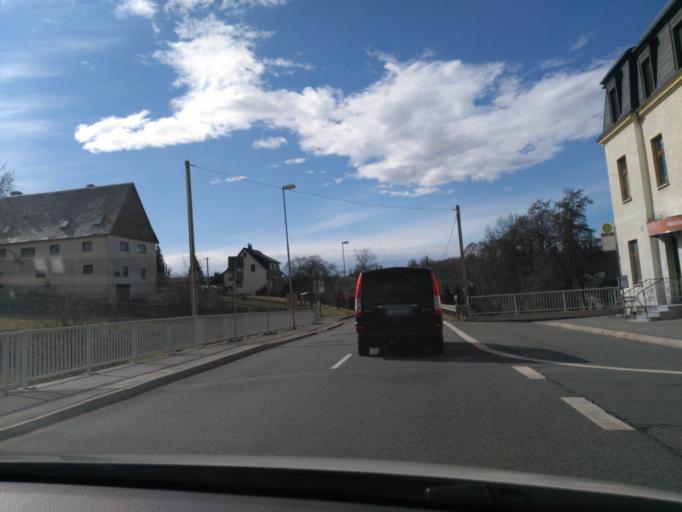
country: DE
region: Saxony
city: Wolkenstein
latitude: 50.6591
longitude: 13.0875
